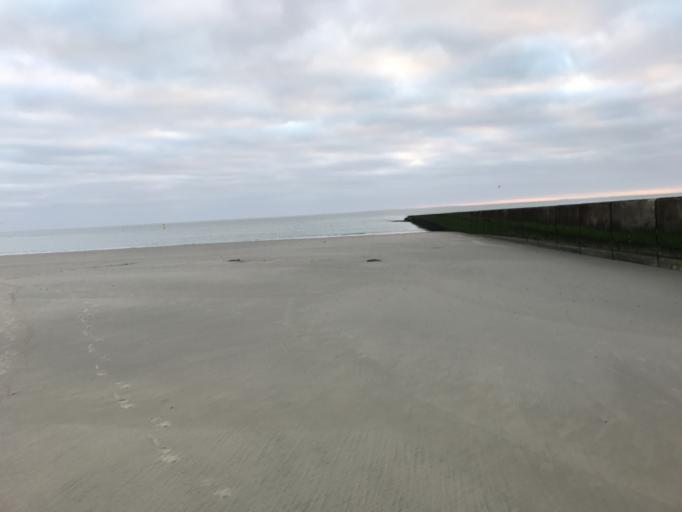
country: DE
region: Lower Saxony
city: Borkum
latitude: 53.5799
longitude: 6.6624
